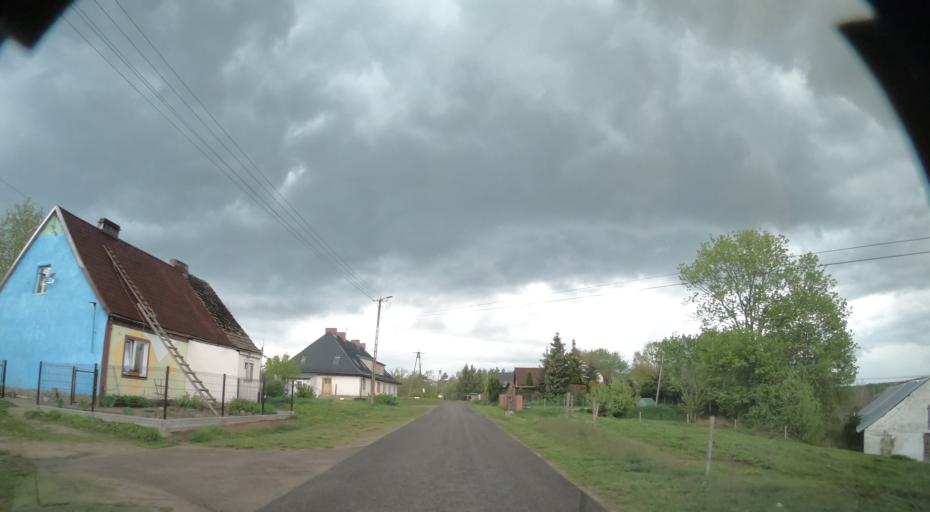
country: PL
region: West Pomeranian Voivodeship
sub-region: Powiat koszalinski
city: Bobolice
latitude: 54.1143
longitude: 16.5018
